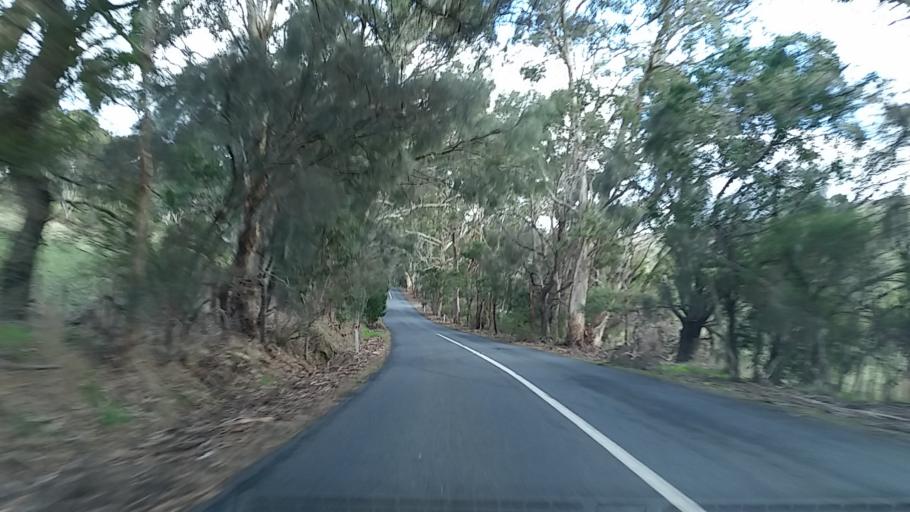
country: AU
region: South Australia
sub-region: Mount Barker
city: Little Hampton
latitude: -35.0756
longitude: 138.8141
